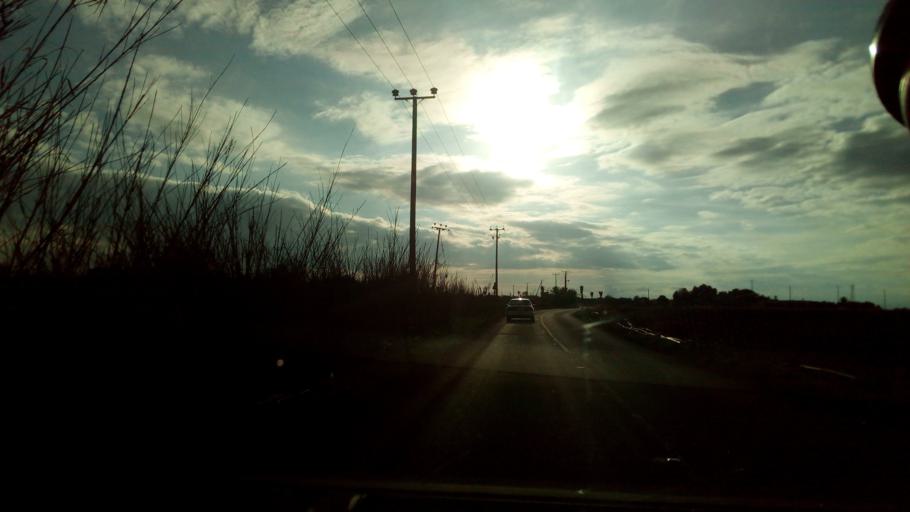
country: CY
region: Ammochostos
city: Achna
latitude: 35.0018
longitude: 33.7963
